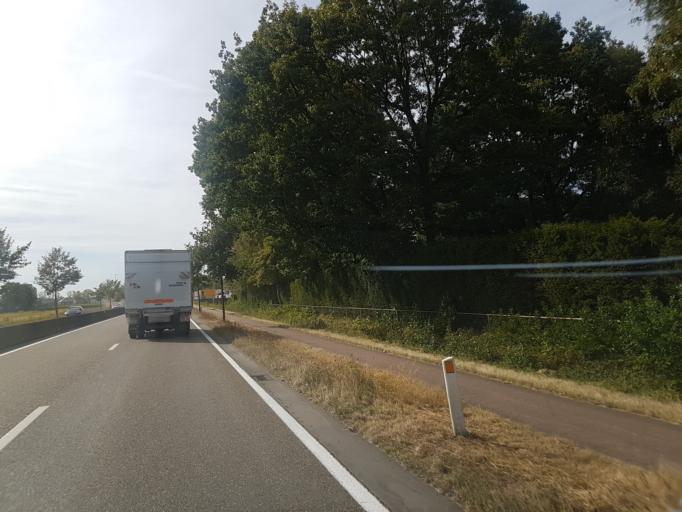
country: BE
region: Flanders
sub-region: Provincie Antwerpen
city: Geel
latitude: 51.1530
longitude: 5.0022
